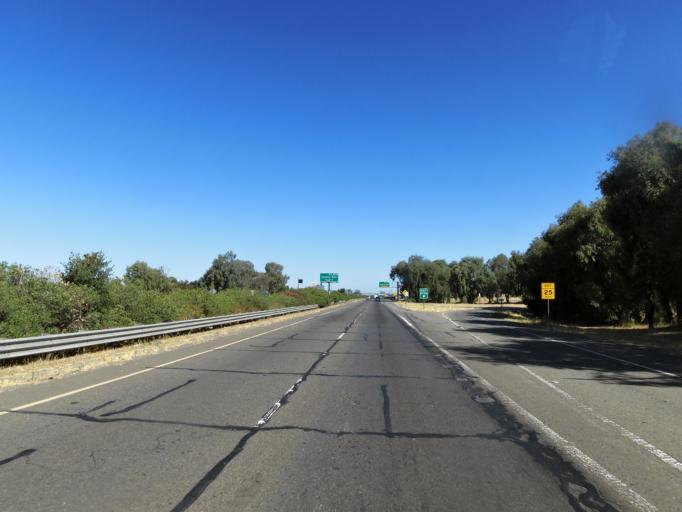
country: US
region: California
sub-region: Sacramento County
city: Galt
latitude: 38.2471
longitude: -121.2887
